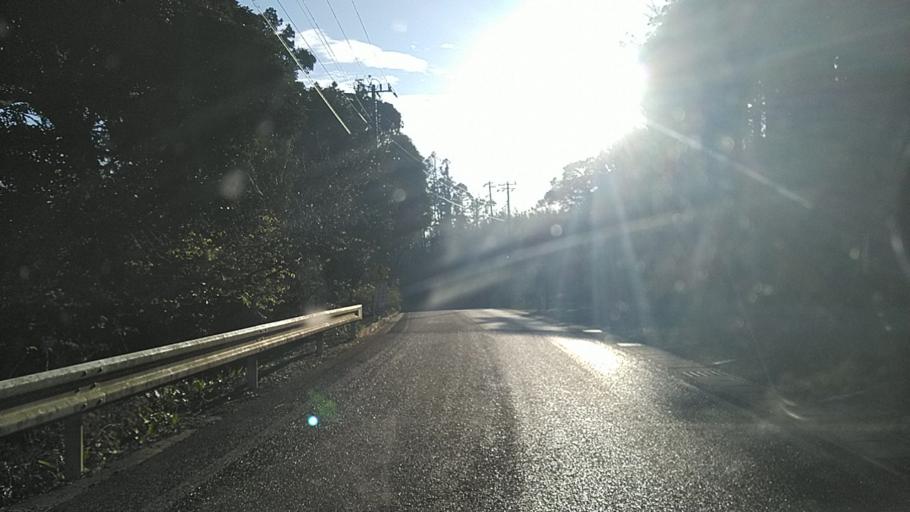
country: JP
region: Chiba
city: Kimitsu
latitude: 35.2537
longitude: 139.9642
